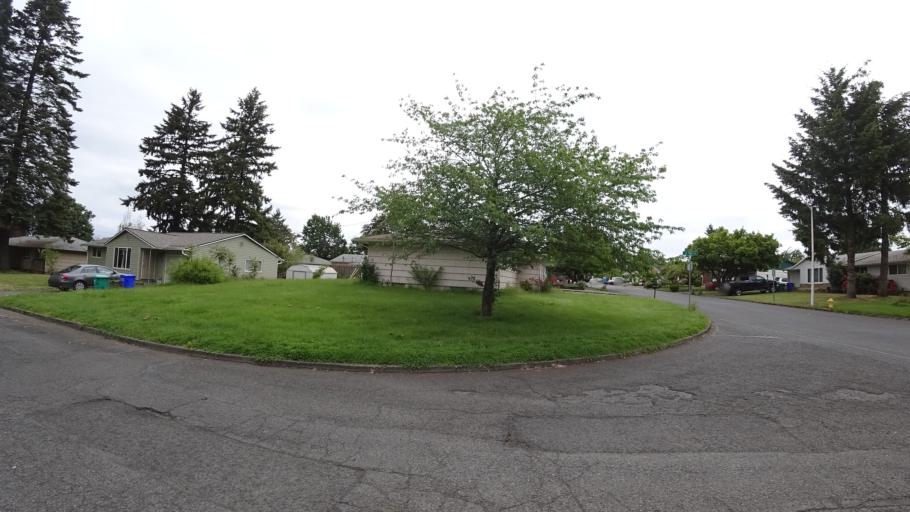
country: US
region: Oregon
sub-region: Multnomah County
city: Gresham
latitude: 45.4976
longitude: -122.4816
